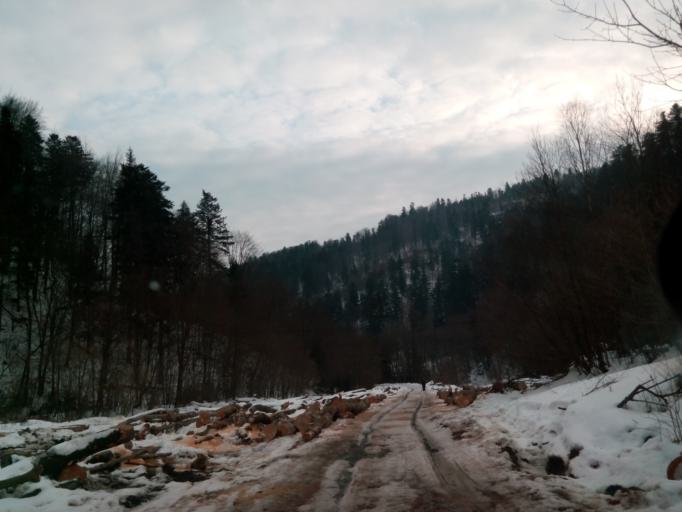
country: SK
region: Presovsky
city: Sabinov
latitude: 49.2035
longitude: 21.0832
